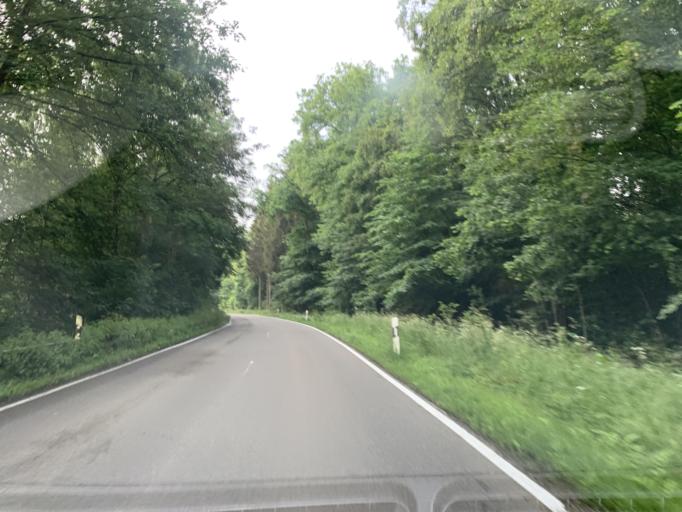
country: DE
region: Baden-Wuerttemberg
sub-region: Tuebingen Region
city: Huttisheim
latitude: 48.3201
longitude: 9.9357
